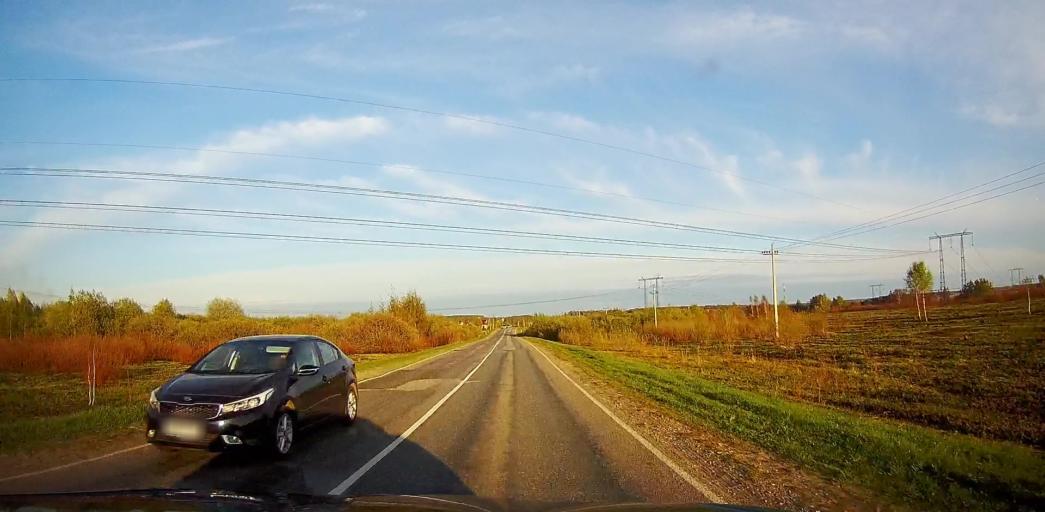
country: RU
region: Moskovskaya
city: Meshcherino
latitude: 55.2641
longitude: 38.2582
